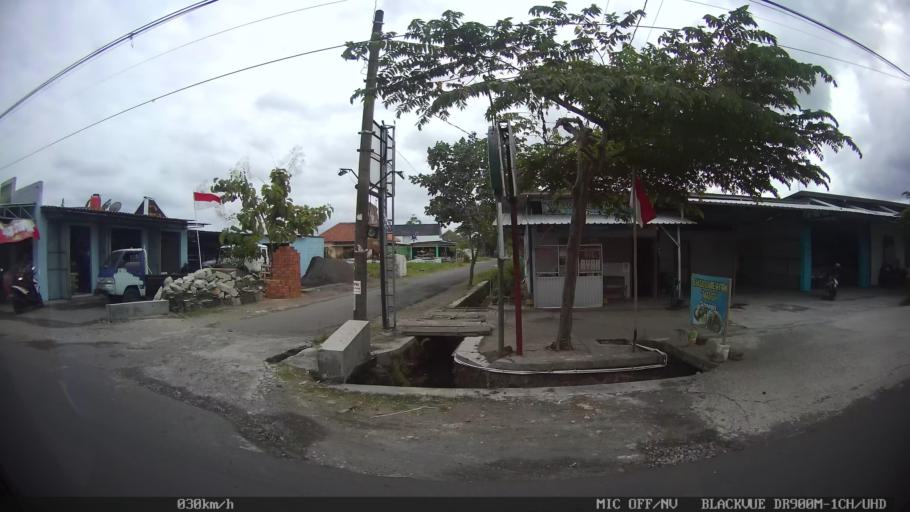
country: ID
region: Daerah Istimewa Yogyakarta
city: Depok
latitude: -7.8298
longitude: 110.4173
